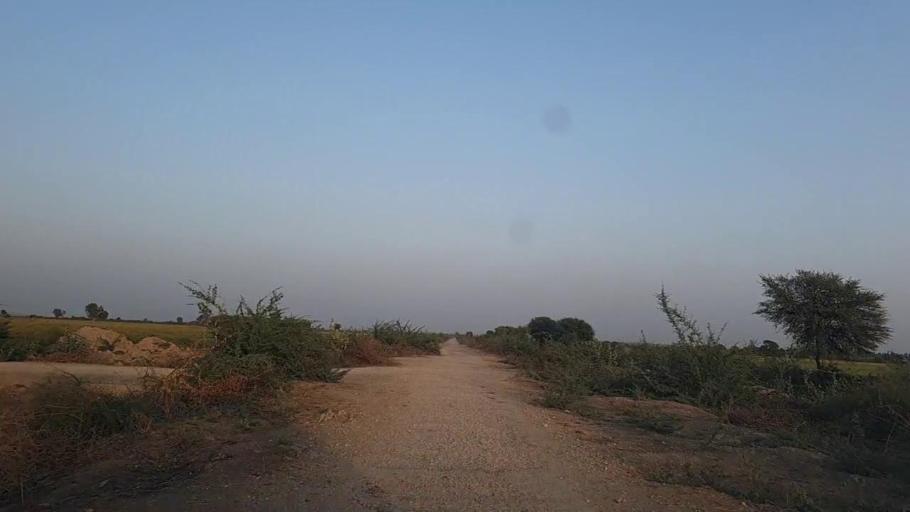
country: PK
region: Sindh
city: Naukot
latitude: 24.6959
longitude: 69.2729
